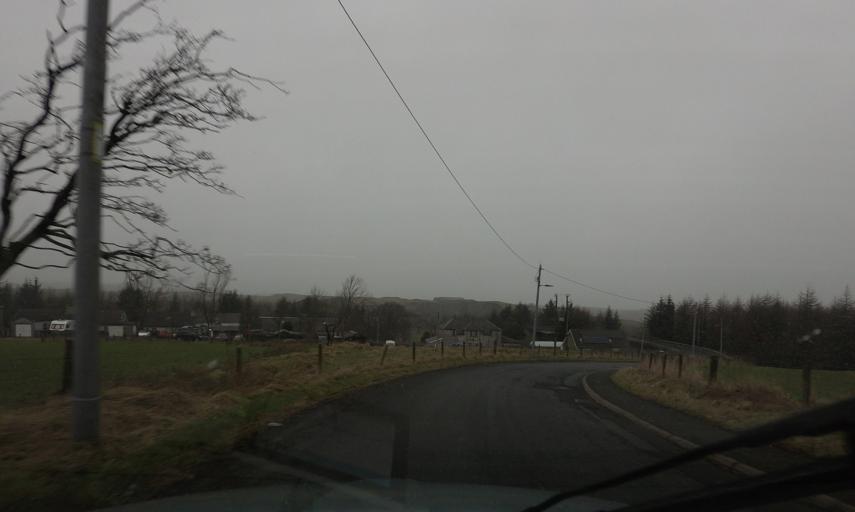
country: GB
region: Scotland
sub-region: North Lanarkshire
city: Shotts
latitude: 55.8529
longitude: -3.8290
